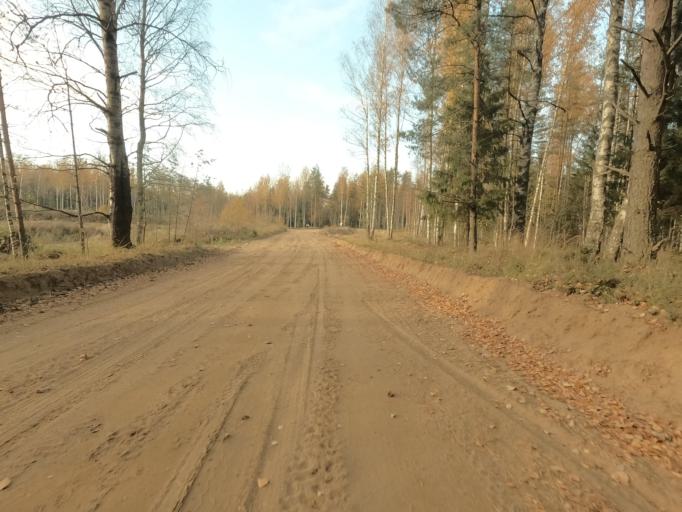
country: RU
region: Leningrad
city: Priladozhskiy
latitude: 59.7384
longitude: 31.3175
